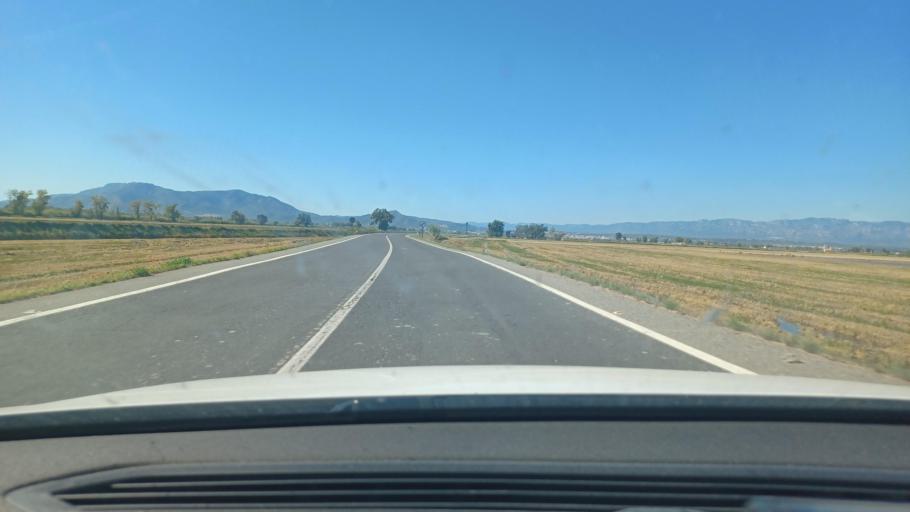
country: ES
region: Catalonia
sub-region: Provincia de Tarragona
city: Deltebre
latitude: 40.7221
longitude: 0.6541
